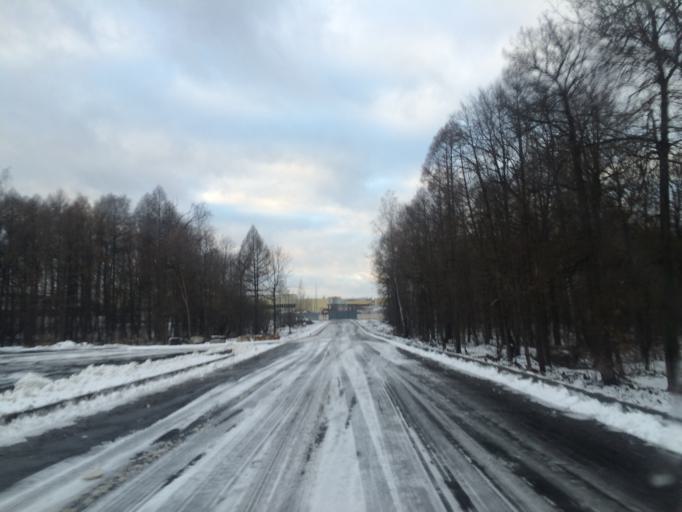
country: RU
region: Tula
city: Tula
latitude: 54.2214
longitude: 37.7072
